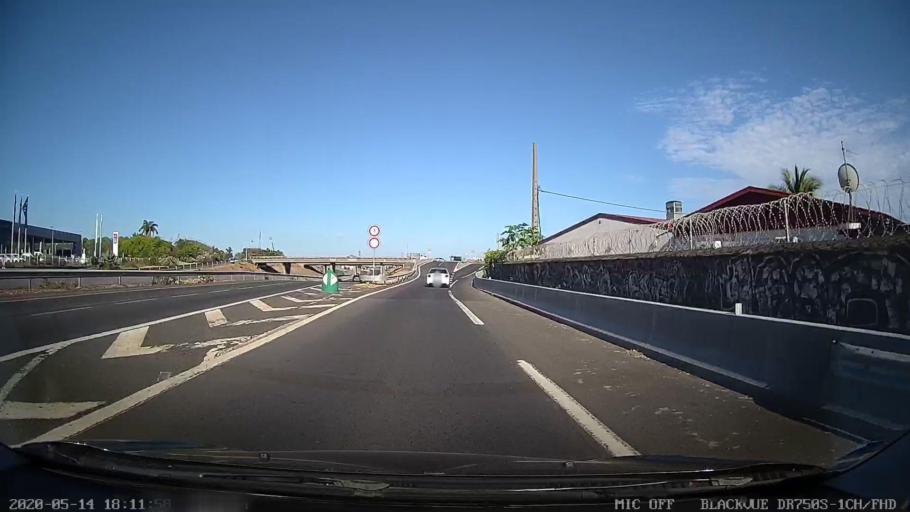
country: RE
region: Reunion
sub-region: Reunion
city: Le Port
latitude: -20.9547
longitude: 55.3130
